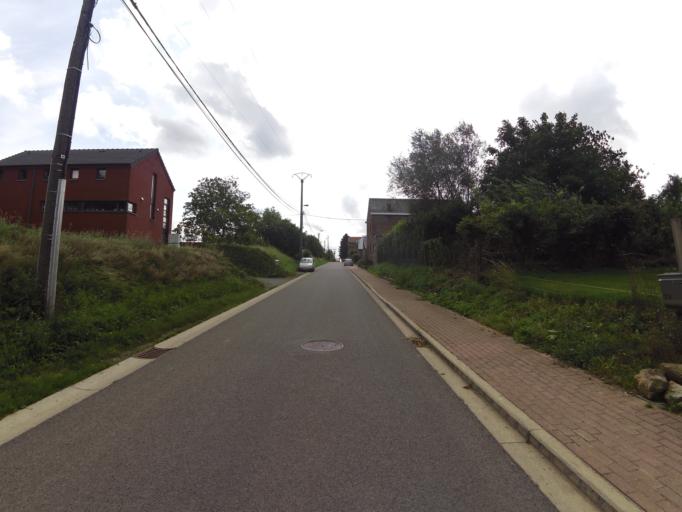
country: BE
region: Wallonia
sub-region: Province de Liege
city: Amay
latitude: 50.5743
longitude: 5.3215
